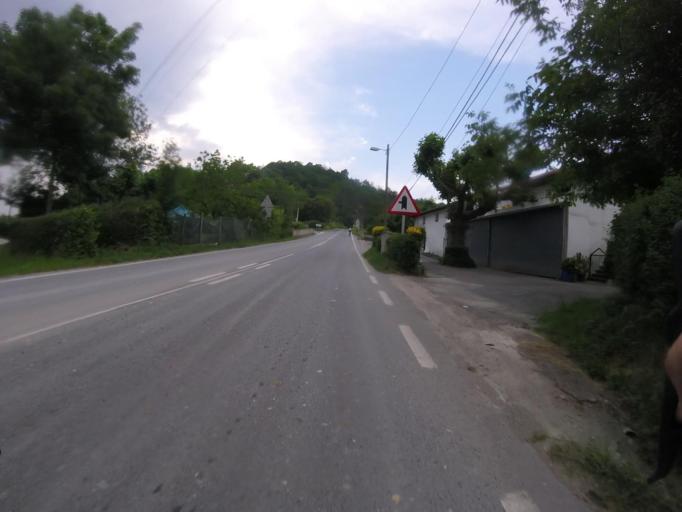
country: ES
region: Basque Country
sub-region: Provincia de Guipuzcoa
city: Errenteria
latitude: 43.2824
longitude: -1.9137
